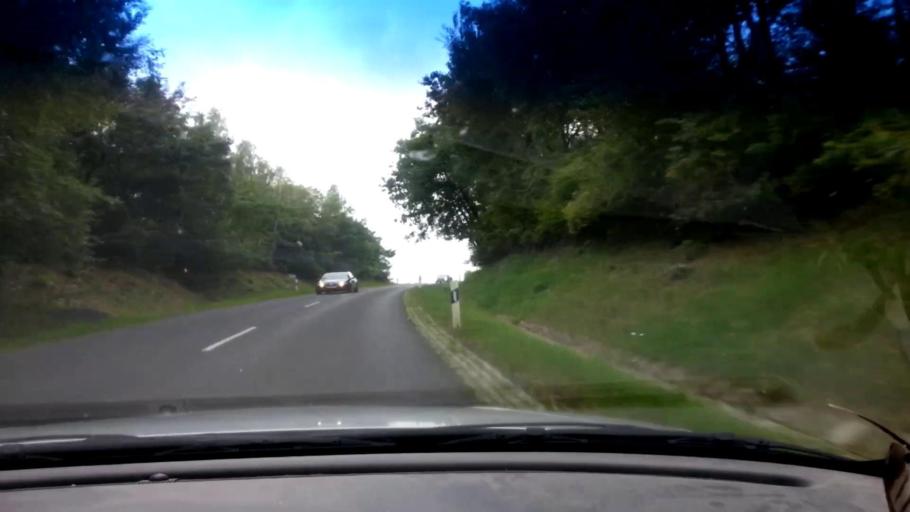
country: DE
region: Bavaria
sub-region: Upper Palatinate
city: Waldsassen
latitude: 50.0338
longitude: 12.2823
